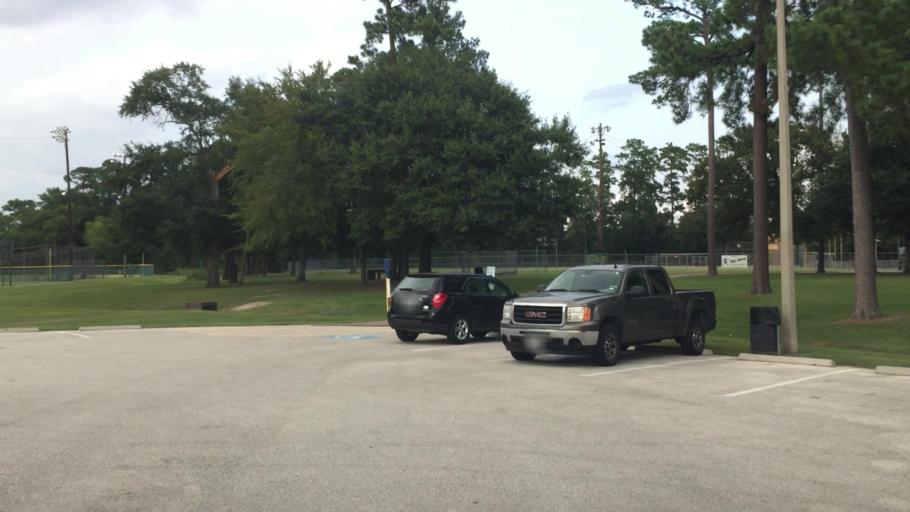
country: US
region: Texas
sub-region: Harris County
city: Hudson
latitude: 30.0113
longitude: -95.5069
